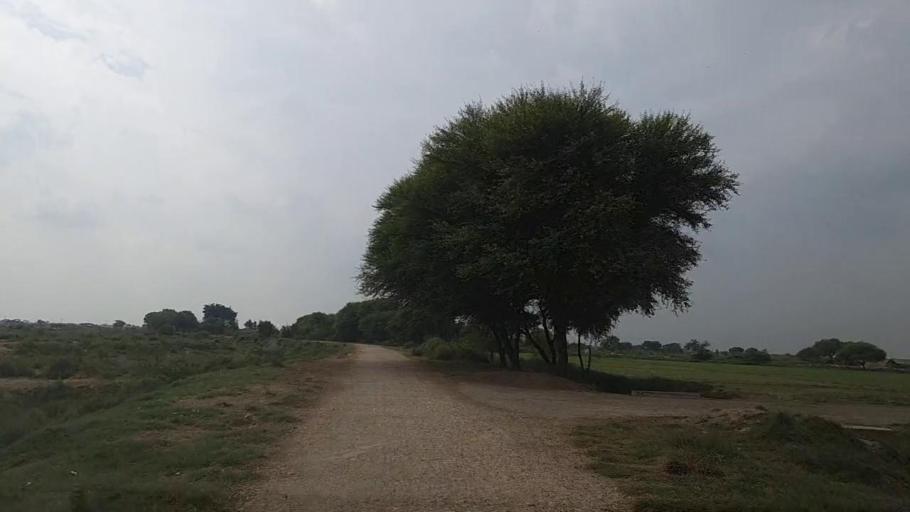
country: PK
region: Sindh
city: Mirpur Batoro
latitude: 24.5898
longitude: 68.1253
